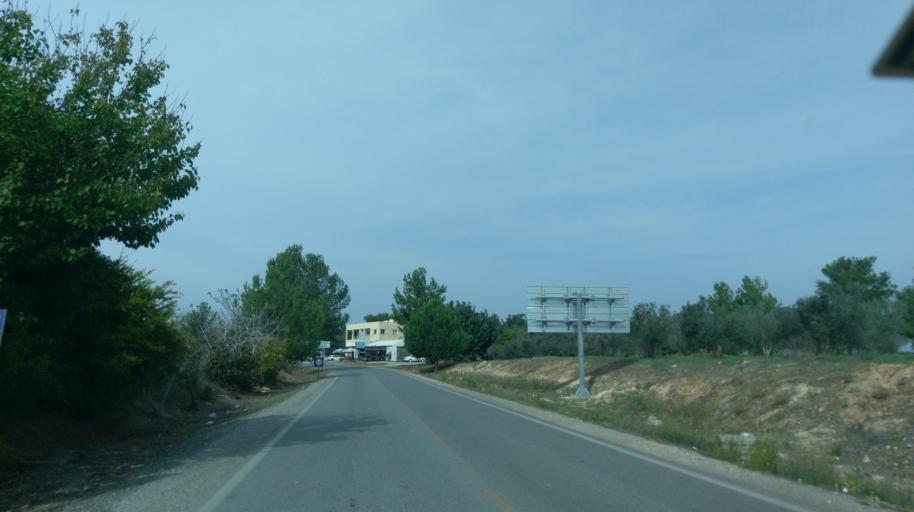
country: CY
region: Keryneia
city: Lapithos
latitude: 35.3134
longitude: 33.0725
